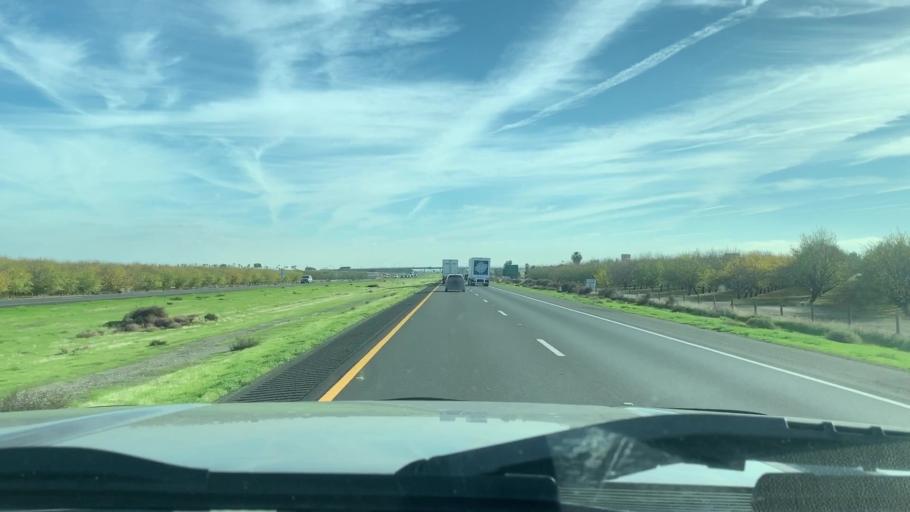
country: US
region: California
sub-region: Fresno County
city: Huron
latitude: 36.2637
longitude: -120.2501
